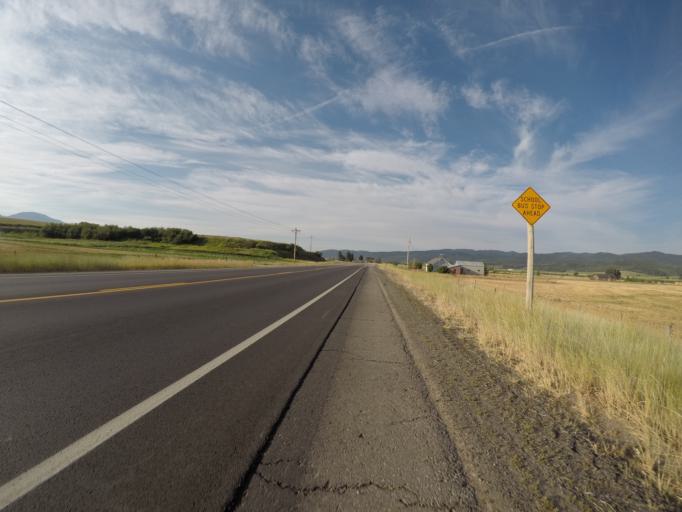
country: US
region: Wyoming
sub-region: Lincoln County
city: Afton
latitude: 42.9555
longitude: -111.0127
